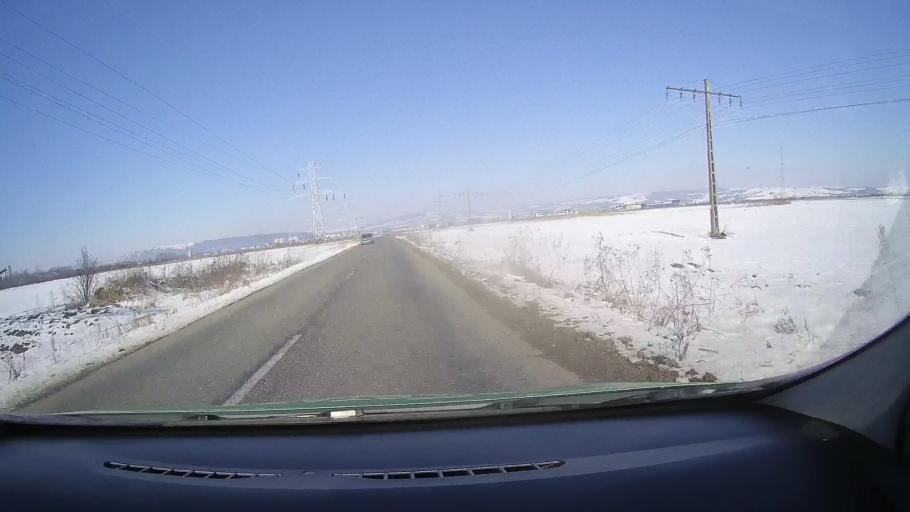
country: RO
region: Brasov
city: Fogarasch
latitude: 45.8127
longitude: 24.9887
